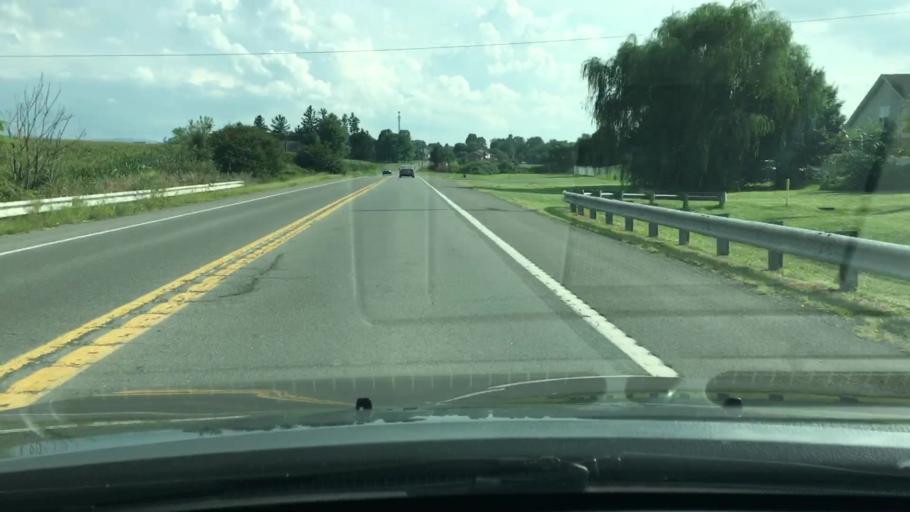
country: US
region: Pennsylvania
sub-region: Franklin County
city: Guilford
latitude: 39.9338
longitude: -77.5906
